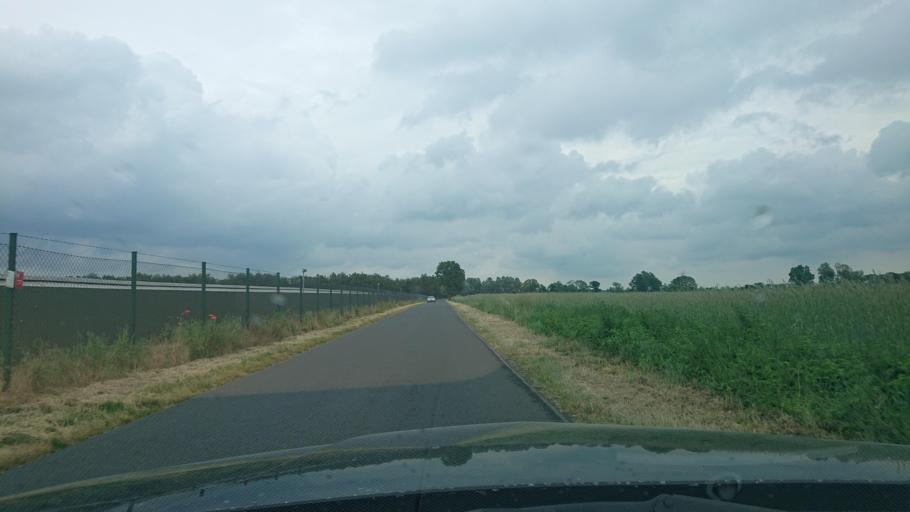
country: PL
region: Greater Poland Voivodeship
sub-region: Powiat gnieznienski
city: Czerniejewo
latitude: 52.4783
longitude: 17.5307
